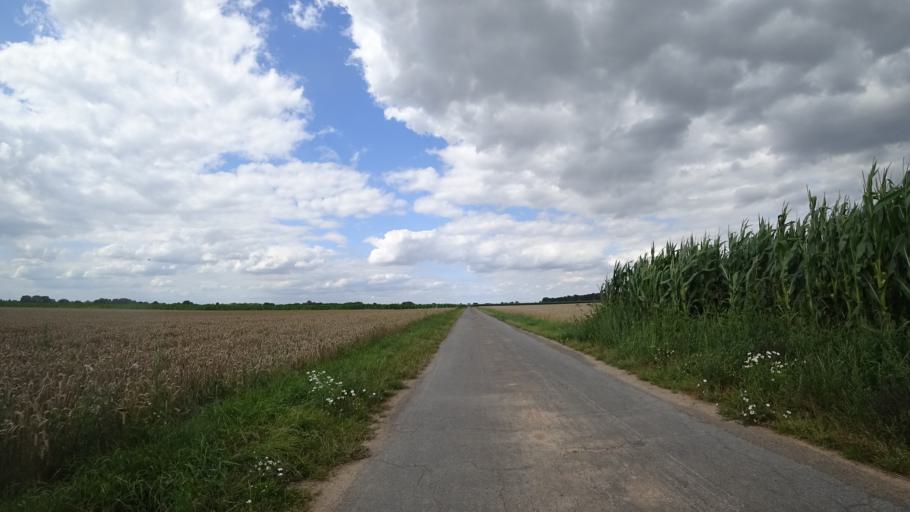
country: DE
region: Lower Saxony
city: Raddestorf
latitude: 52.4384
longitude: 9.0221
